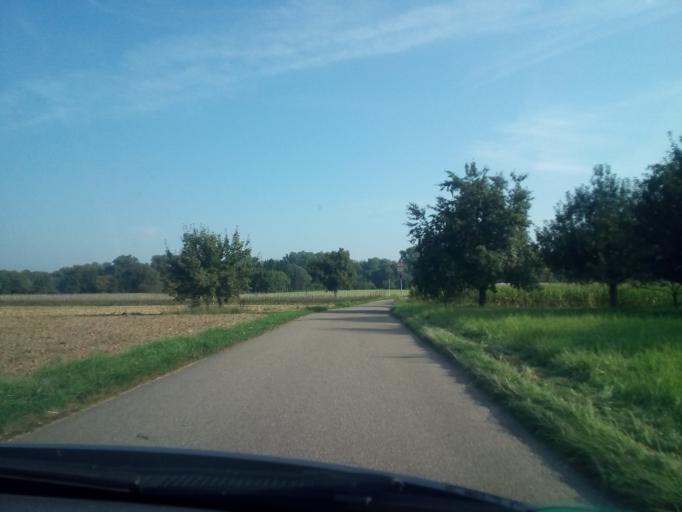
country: DE
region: Baden-Wuerttemberg
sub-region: Karlsruhe Region
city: Lichtenau
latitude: 48.7184
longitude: 7.9848
